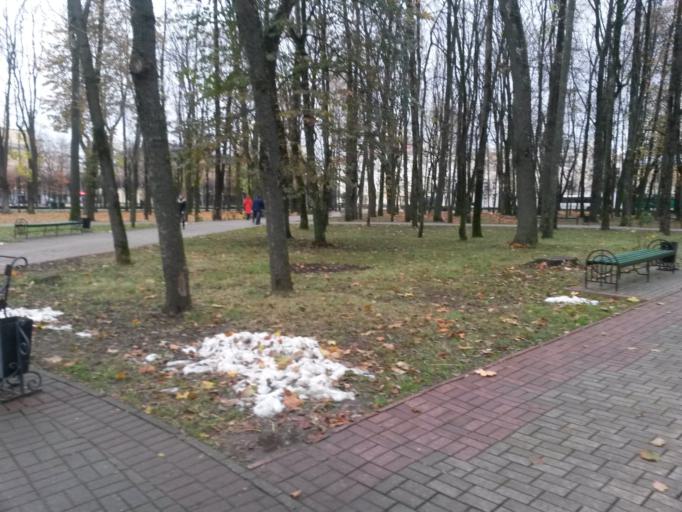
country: RU
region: Smolensk
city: Smolensk
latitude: 54.7814
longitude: 32.0460
